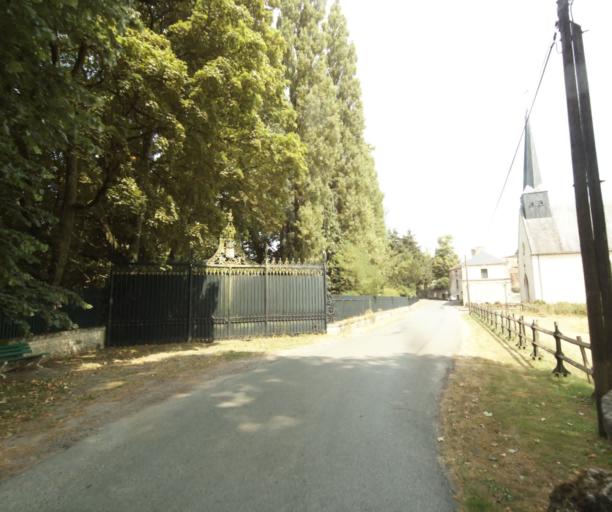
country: FR
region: Centre
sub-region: Departement d'Eure-et-Loir
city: Authon-du-Perche
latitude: 48.1905
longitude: 0.9341
